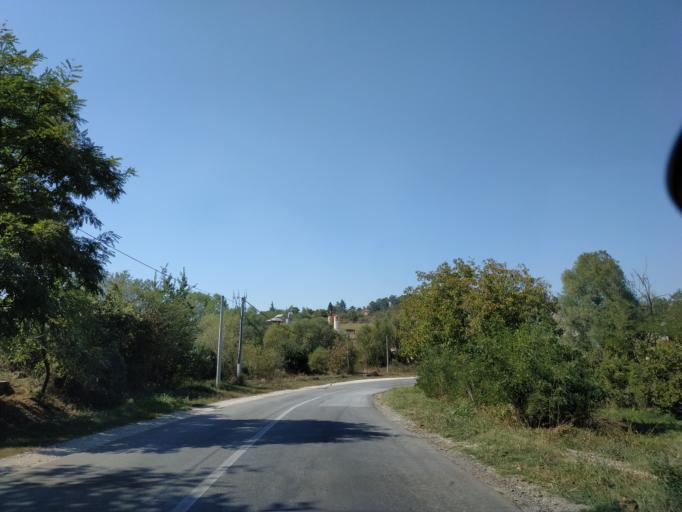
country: RS
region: Central Serbia
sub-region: Sumadijski Okrug
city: Arangelovac
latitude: 44.2845
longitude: 20.6106
